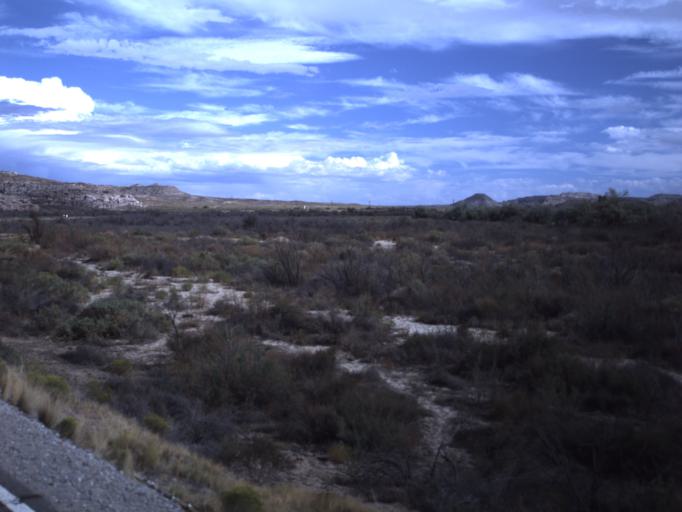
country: US
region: Utah
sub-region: San Juan County
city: Blanding
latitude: 37.2587
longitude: -109.2688
